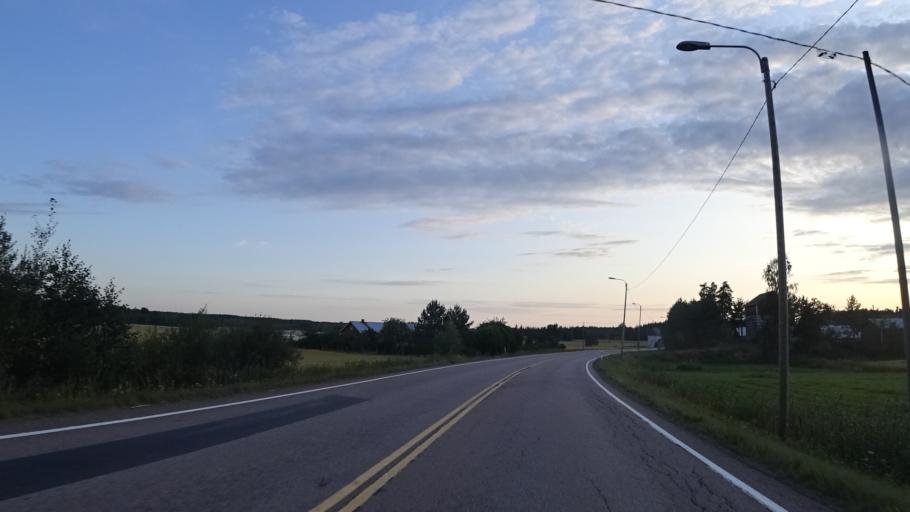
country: FI
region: Kymenlaakso
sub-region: Kotka-Hamina
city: Miehikkaelae
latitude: 60.6383
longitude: 27.8751
